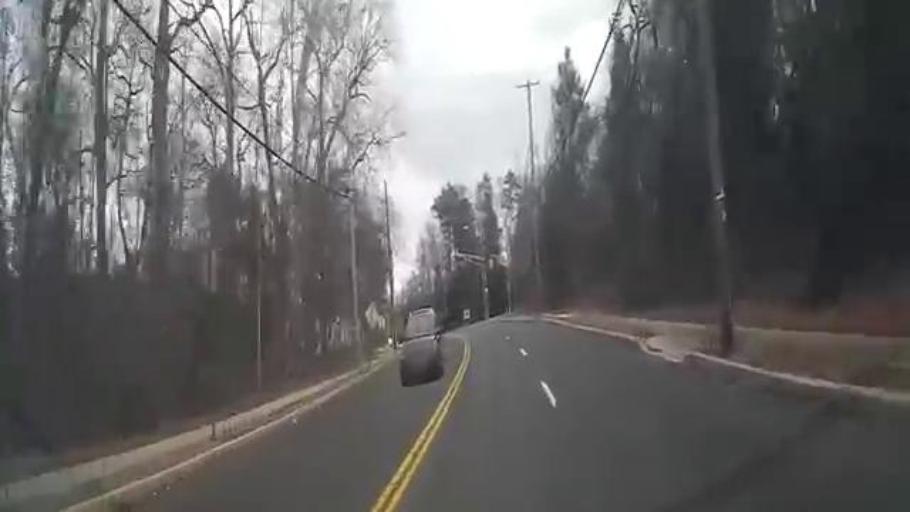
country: US
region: New Jersey
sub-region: Camden County
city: Clementon
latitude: 39.7998
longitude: -74.9671
